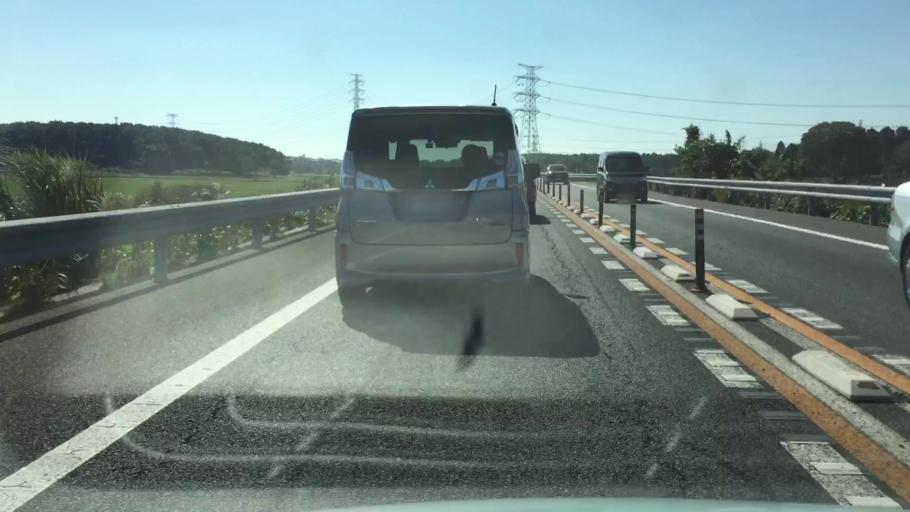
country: JP
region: Ibaraki
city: Ushiku
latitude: 36.0105
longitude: 140.1432
